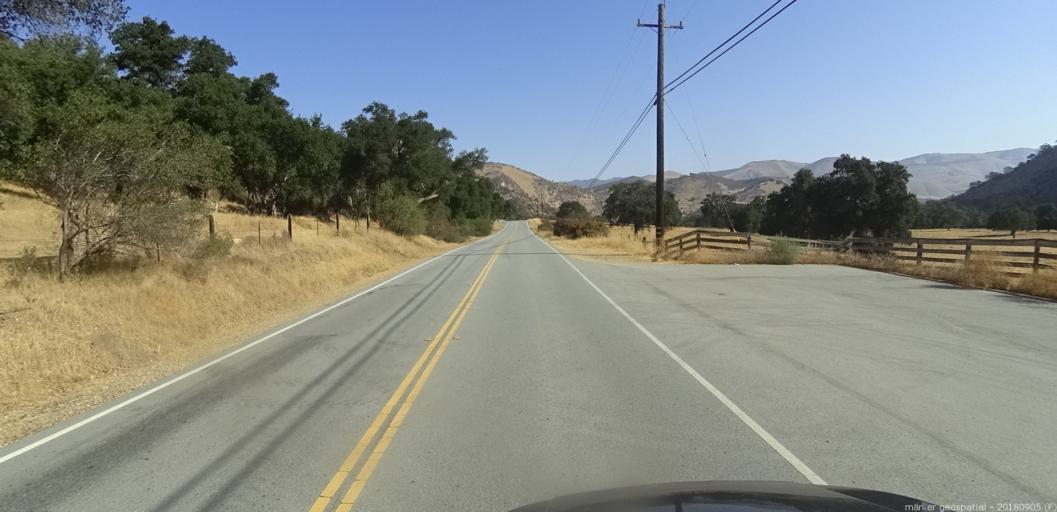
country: US
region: California
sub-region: Monterey County
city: Greenfield
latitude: 36.2438
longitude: -121.4323
